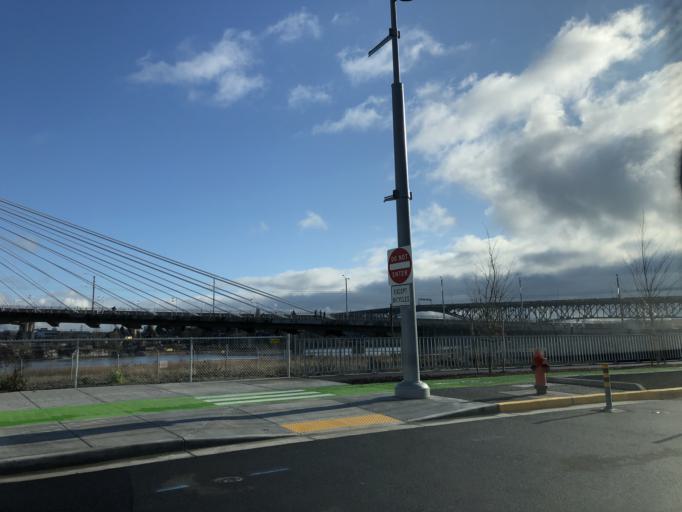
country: US
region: Oregon
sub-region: Multnomah County
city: Portland
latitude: 45.5041
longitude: -122.6704
